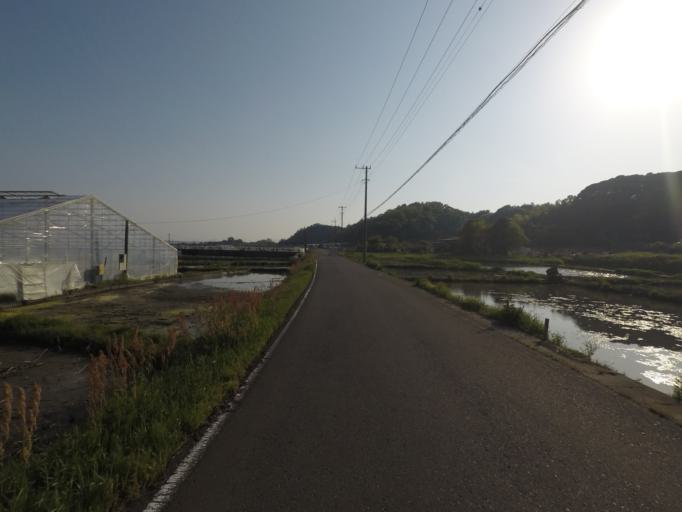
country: JP
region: Ibaraki
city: Ami
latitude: 36.0695
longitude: 140.2988
